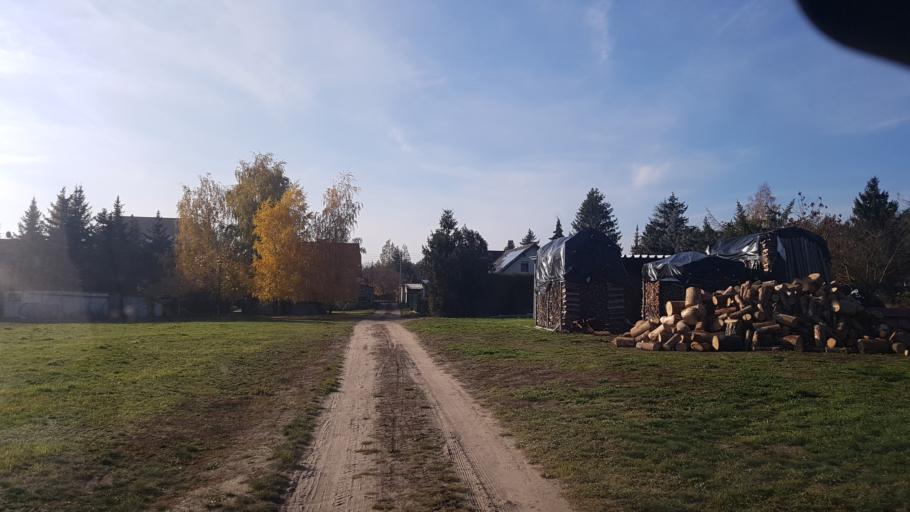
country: DE
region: Brandenburg
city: Schilda
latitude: 51.6485
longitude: 13.3883
